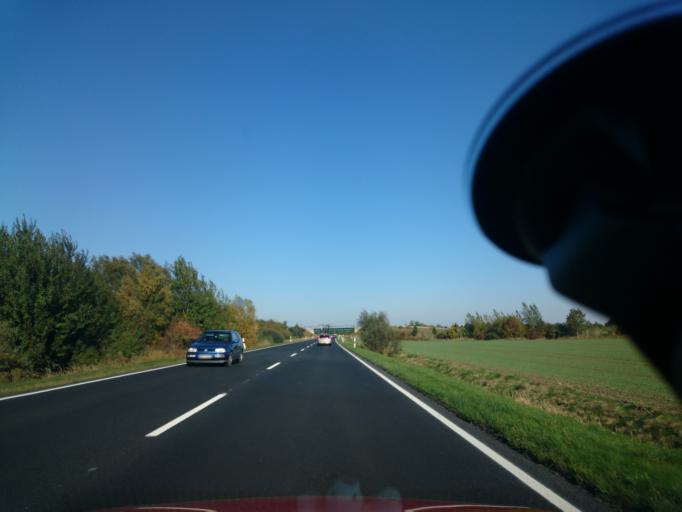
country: DE
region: Mecklenburg-Vorpommern
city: Bentwisch
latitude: 54.1234
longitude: 12.2031
